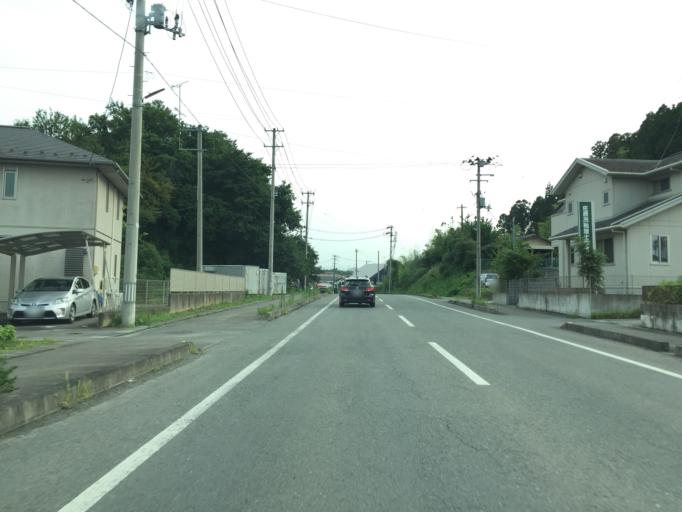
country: JP
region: Miyagi
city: Marumori
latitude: 37.8012
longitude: 140.9125
